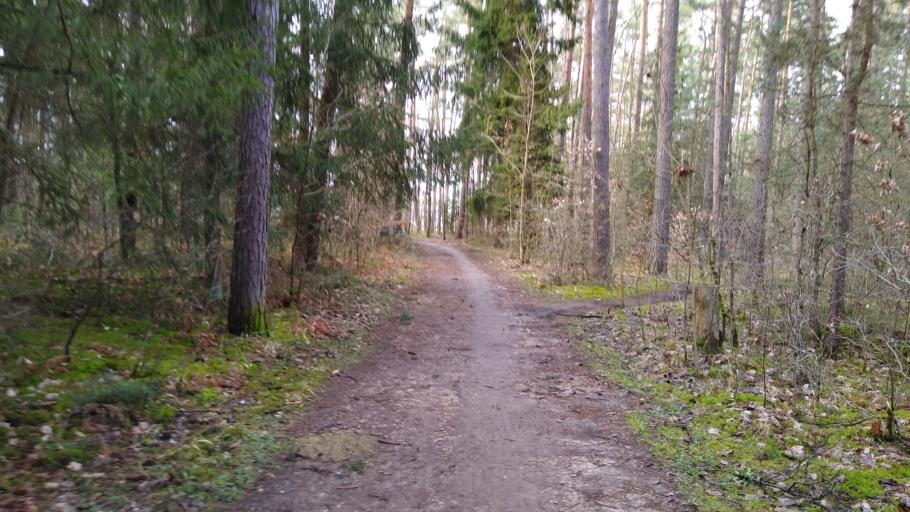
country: DE
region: Bavaria
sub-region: Regierungsbezirk Mittelfranken
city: Heroldsberg
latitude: 49.4864
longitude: 11.1333
